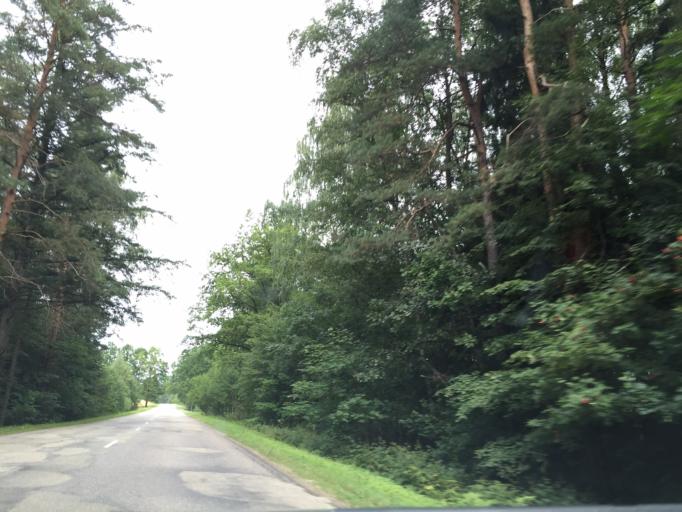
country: LV
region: Ogre
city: Ogre
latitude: 56.8764
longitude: 24.5697
